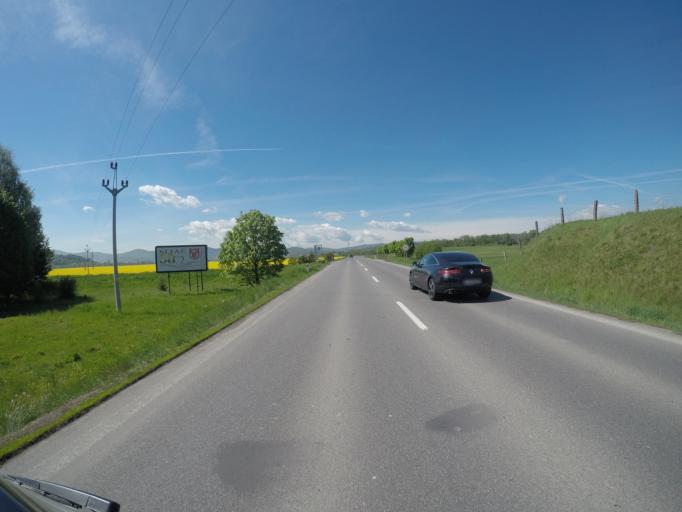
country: SK
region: Banskobystricky
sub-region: Okres Banska Bystrica
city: Zvolen
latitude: 48.6117
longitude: 19.1302
